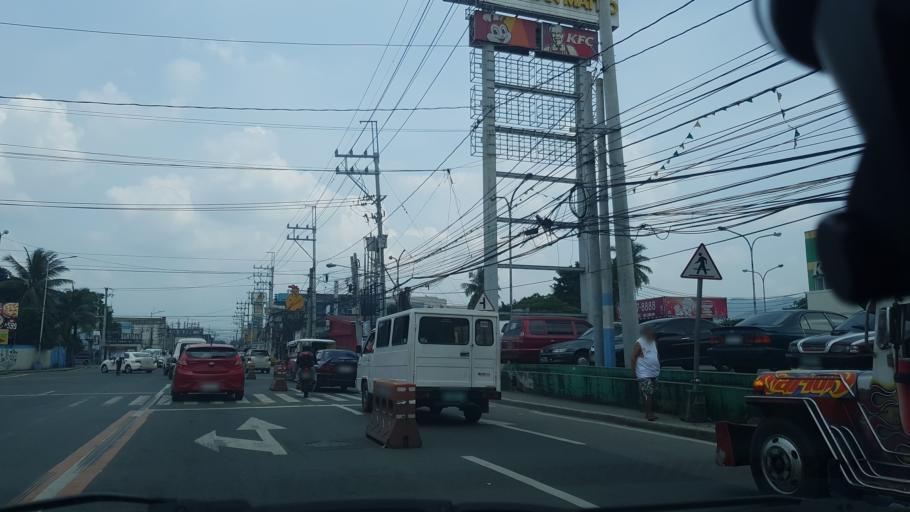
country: PH
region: Calabarzon
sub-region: Province of Rizal
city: San Mateo
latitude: 14.6775
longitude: 121.1115
